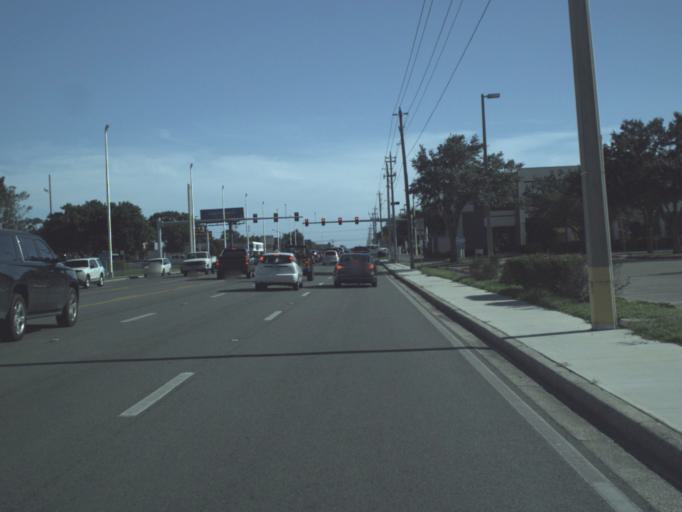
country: US
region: Florida
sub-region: Manatee County
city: Bayshore Gardens
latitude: 27.4327
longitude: -82.5756
